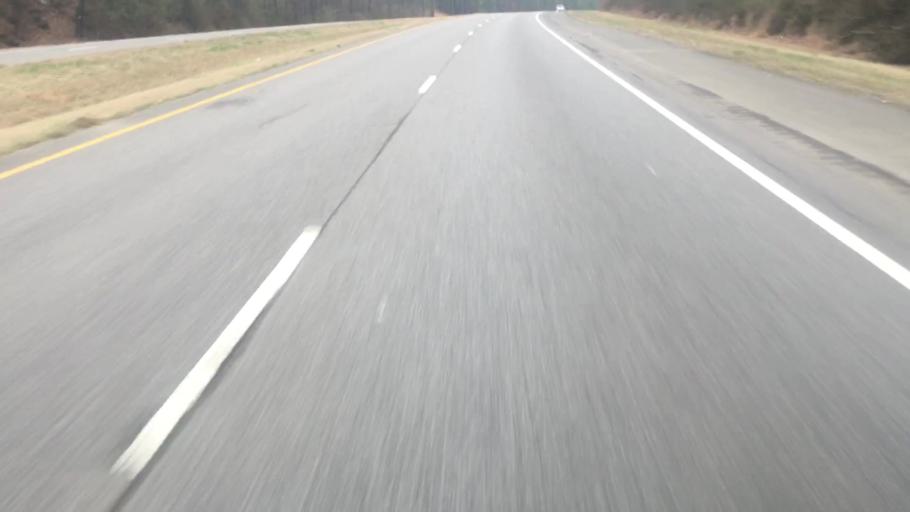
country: US
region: Alabama
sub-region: Jefferson County
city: Graysville
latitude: 33.6882
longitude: -86.9770
